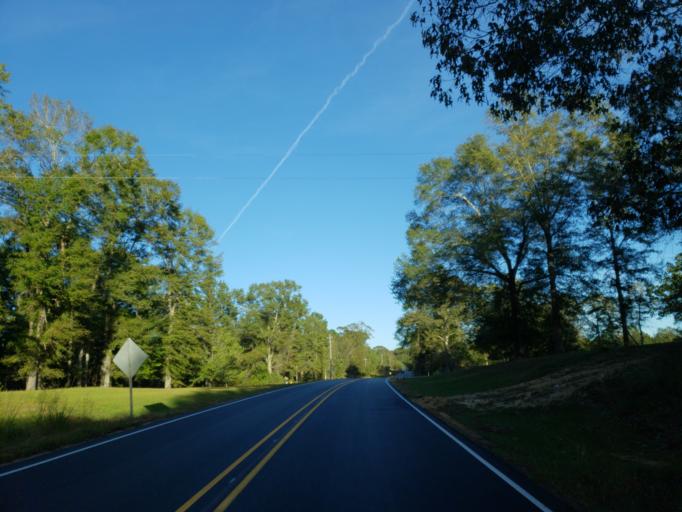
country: US
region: Mississippi
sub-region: Perry County
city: Richton
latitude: 31.3468
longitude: -88.7722
